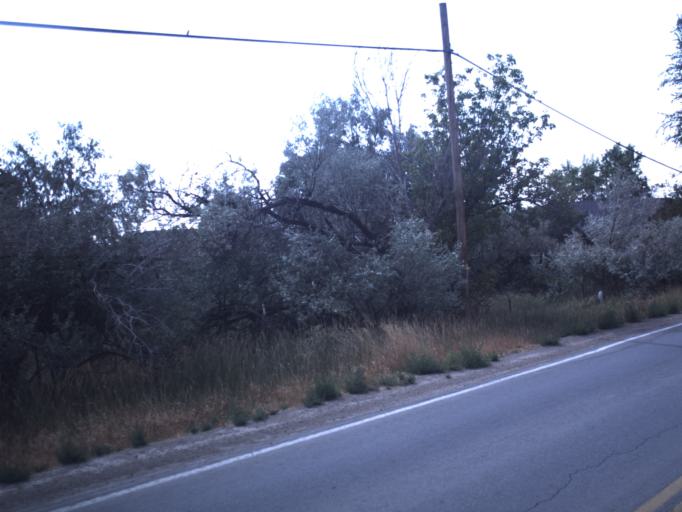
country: US
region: Utah
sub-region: Uintah County
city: Naples
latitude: 40.3910
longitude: -109.4988
